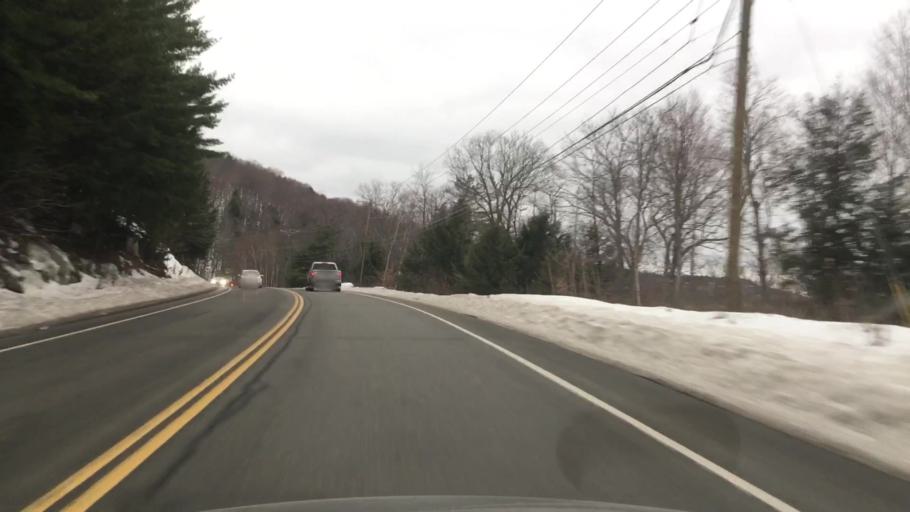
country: US
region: New Hampshire
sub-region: Merrimack County
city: Newbury
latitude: 43.3354
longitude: -72.0512
